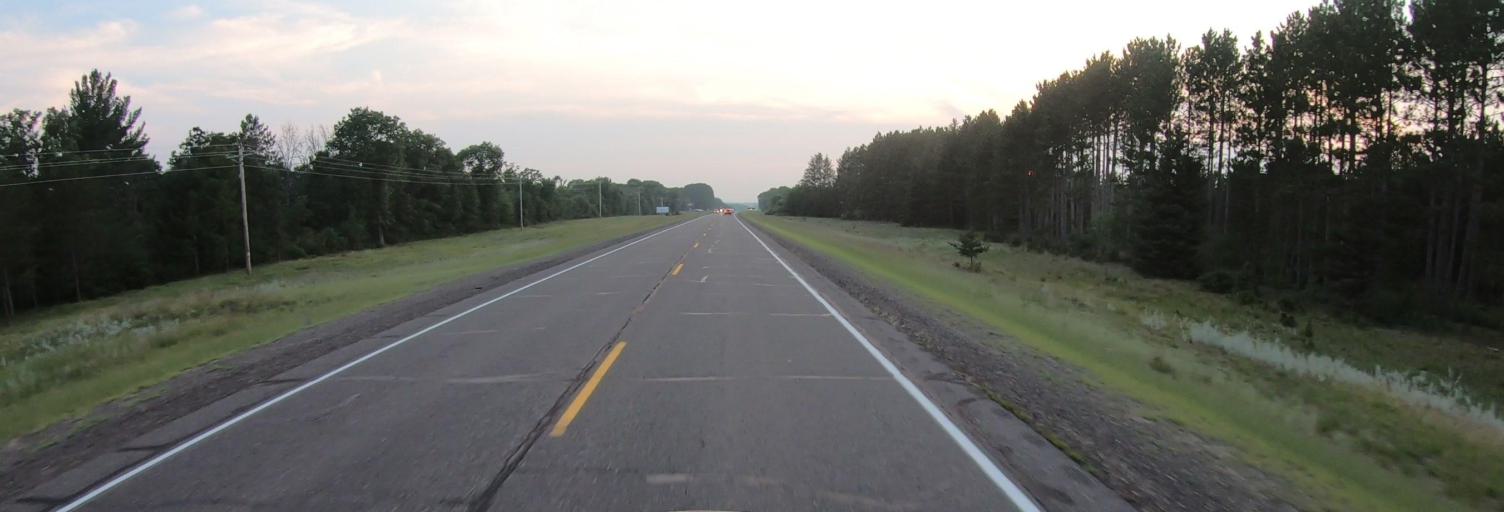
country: US
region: Wisconsin
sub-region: Burnett County
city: Grantsburg
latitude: 45.7730
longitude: -92.7570
